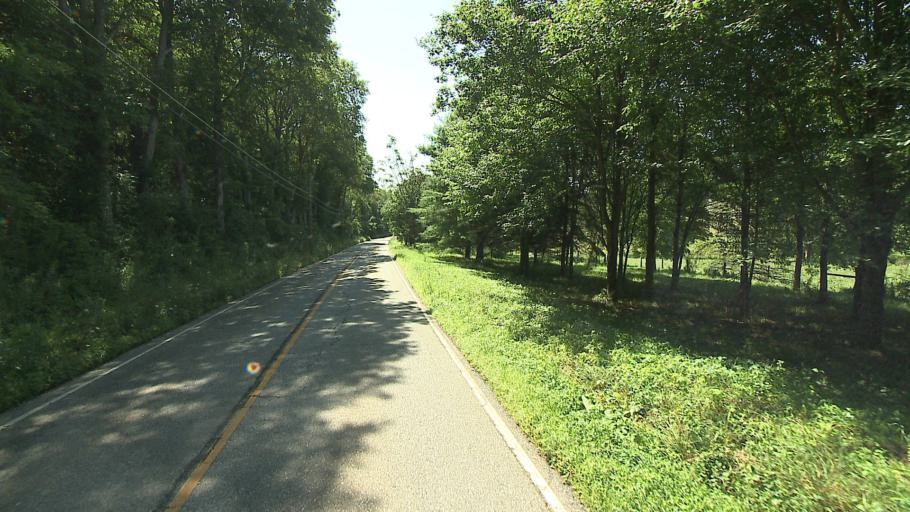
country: US
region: Connecticut
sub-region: Litchfield County
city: Kent
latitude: 41.9017
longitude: -73.4893
